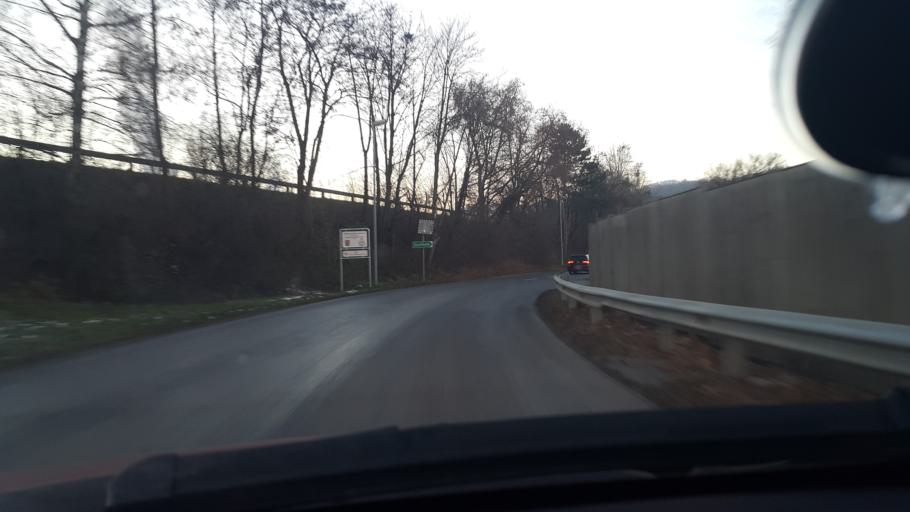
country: AT
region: Styria
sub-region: Politischer Bezirk Graz-Umgebung
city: Gratkorn
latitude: 47.1335
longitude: 15.3443
